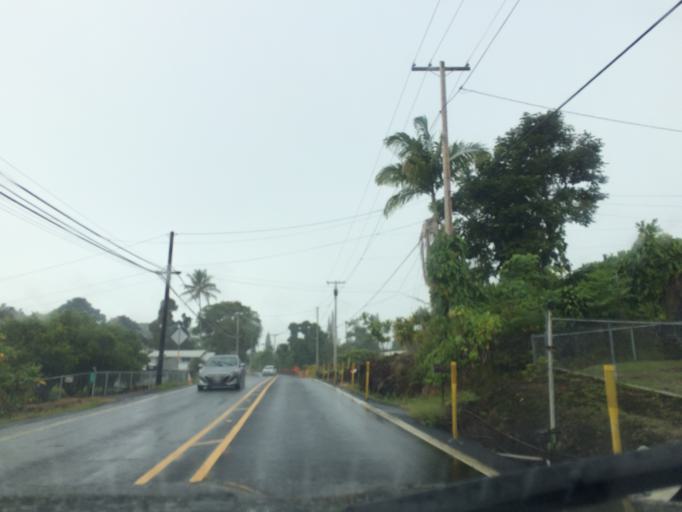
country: US
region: Hawaii
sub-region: Hawaii County
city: Hilo
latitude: 19.6966
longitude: -155.1174
